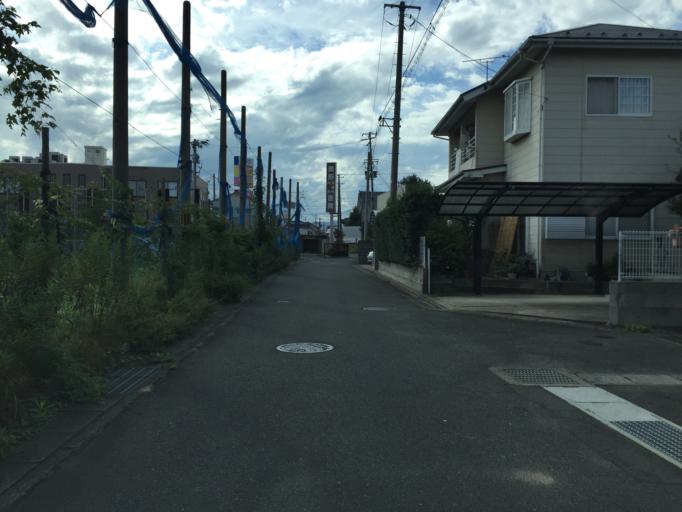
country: JP
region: Fukushima
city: Hobaramachi
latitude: 37.8030
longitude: 140.4938
